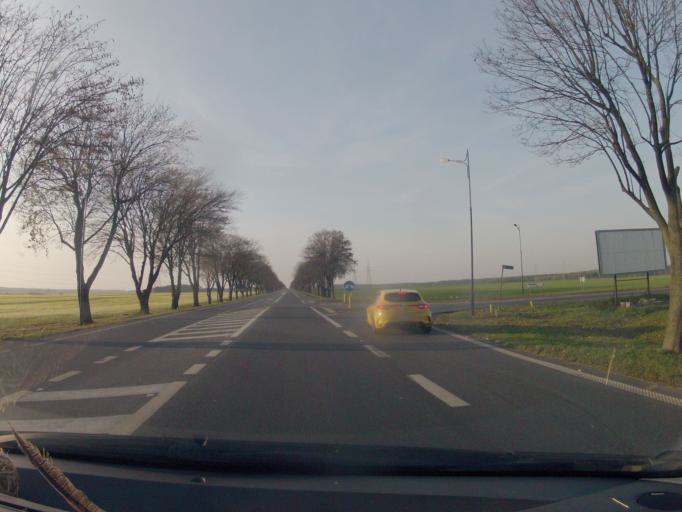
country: PL
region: Opole Voivodeship
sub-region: Powiat strzelecki
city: Strzelce Opolskie
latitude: 50.5253
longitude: 18.2737
